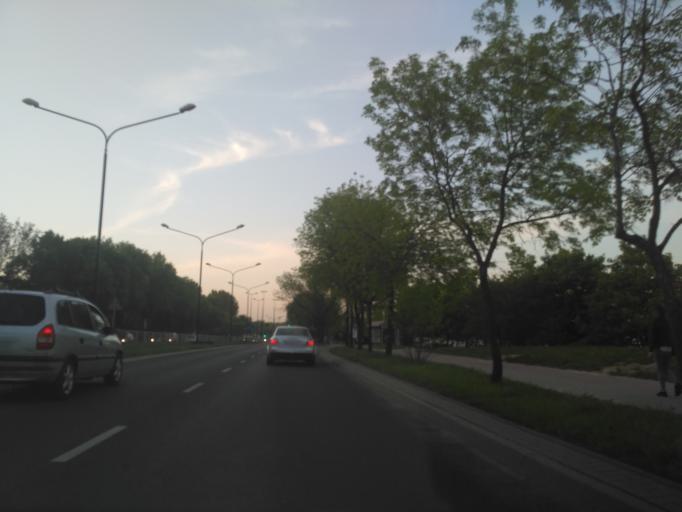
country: PL
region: Lublin Voivodeship
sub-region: Powiat lubelski
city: Lublin
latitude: 51.2654
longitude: 22.5584
